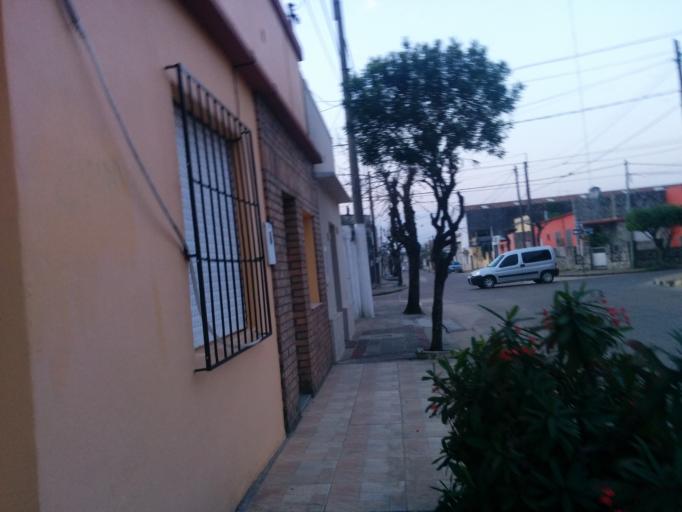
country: AR
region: Entre Rios
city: Concordia
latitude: -31.3866
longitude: -58.0207
